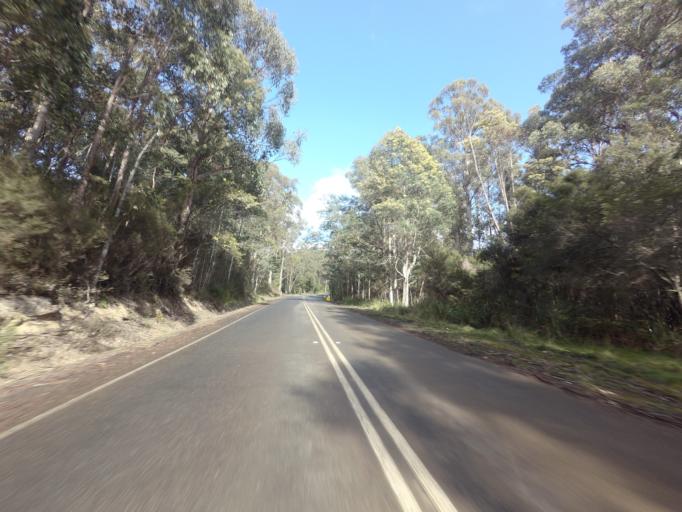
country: AU
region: Tasmania
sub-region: Huon Valley
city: Geeveston
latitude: -43.4132
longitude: 146.9178
